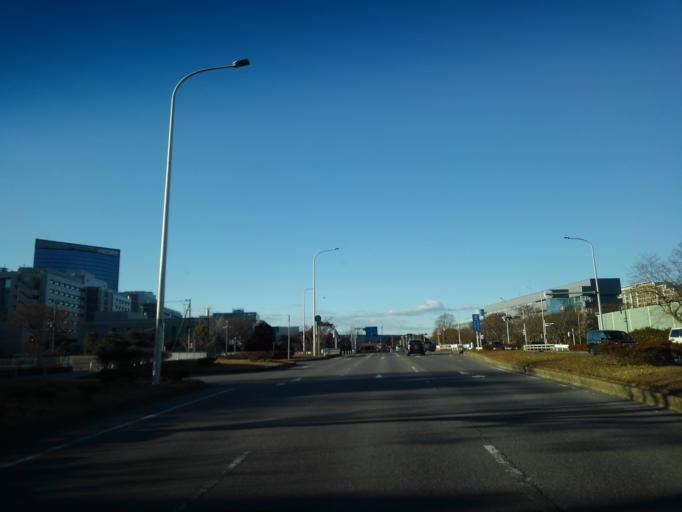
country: JP
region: Chiba
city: Funabashi
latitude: 35.6604
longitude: 140.0416
